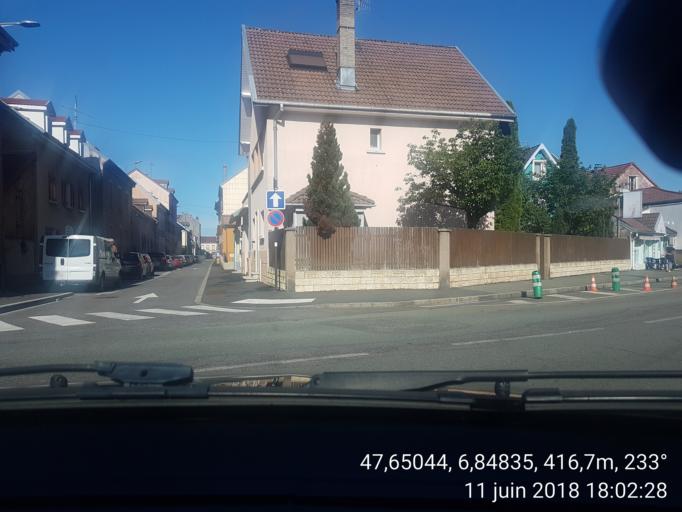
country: FR
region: Franche-Comte
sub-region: Territoire de Belfort
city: Cravanche
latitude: 47.6505
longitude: 6.8483
